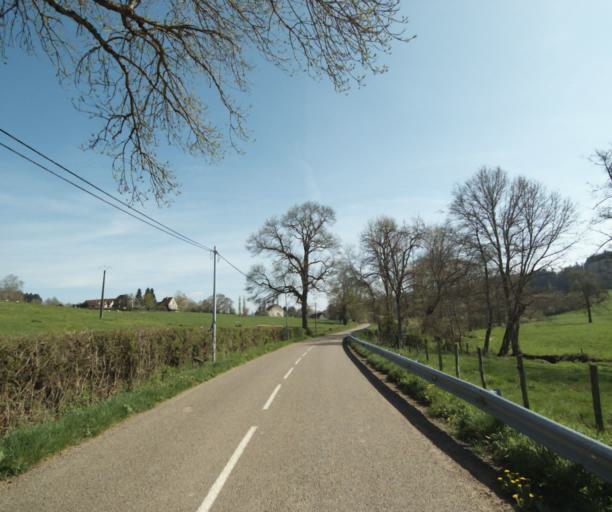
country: FR
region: Bourgogne
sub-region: Departement de Saone-et-Loire
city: Charolles
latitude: 46.3863
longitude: 4.3490
